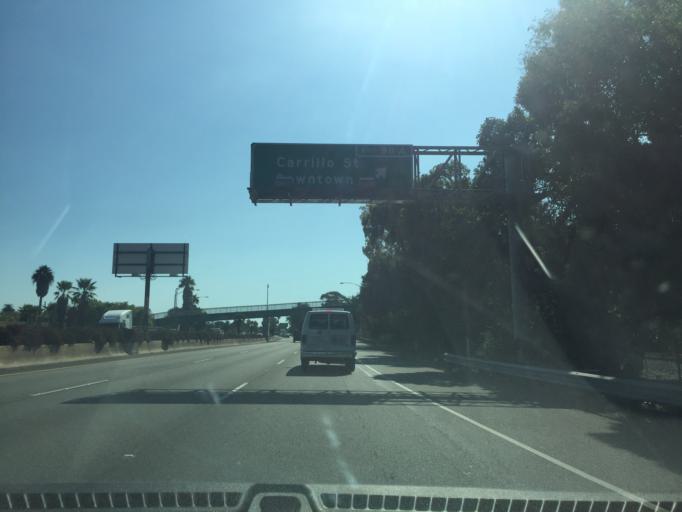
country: US
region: California
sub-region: Santa Barbara County
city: Santa Barbara
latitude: 34.4189
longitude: -119.7114
